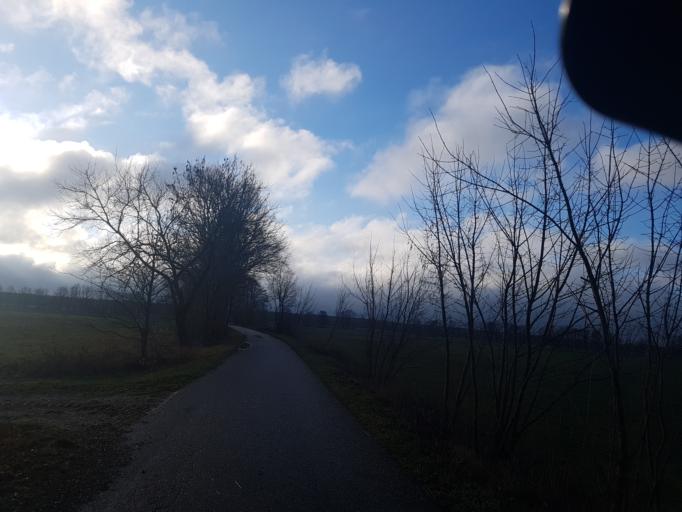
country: DE
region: Brandenburg
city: Ruckersdorf
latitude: 51.5987
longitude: 13.6244
